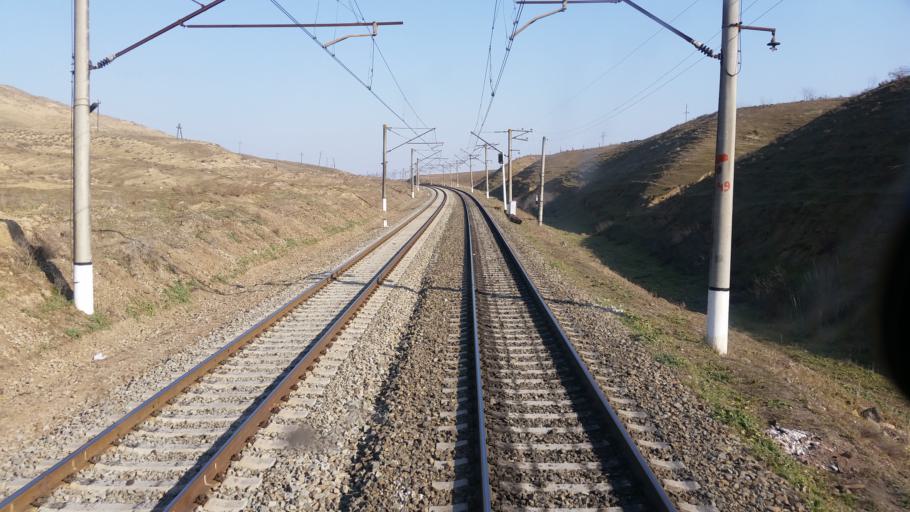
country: AZ
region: Haciqabul
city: Haciqabul
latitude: 40.0464
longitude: 48.9706
